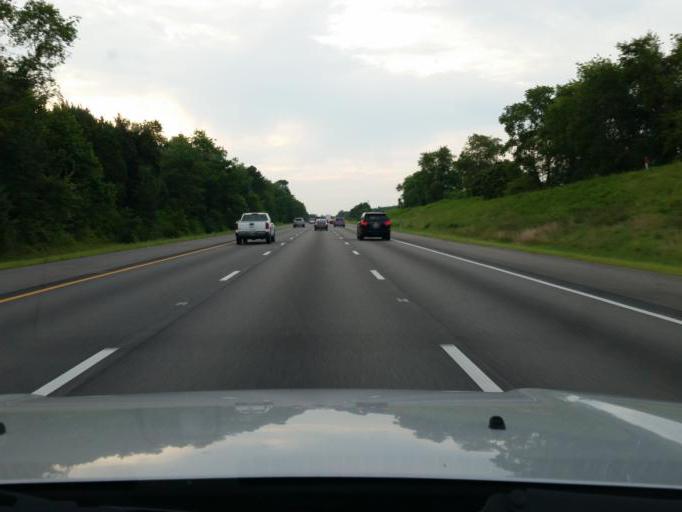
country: US
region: Virginia
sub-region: Spotsylvania County
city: Spotsylvania Courthouse
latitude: 38.0730
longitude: -77.5105
